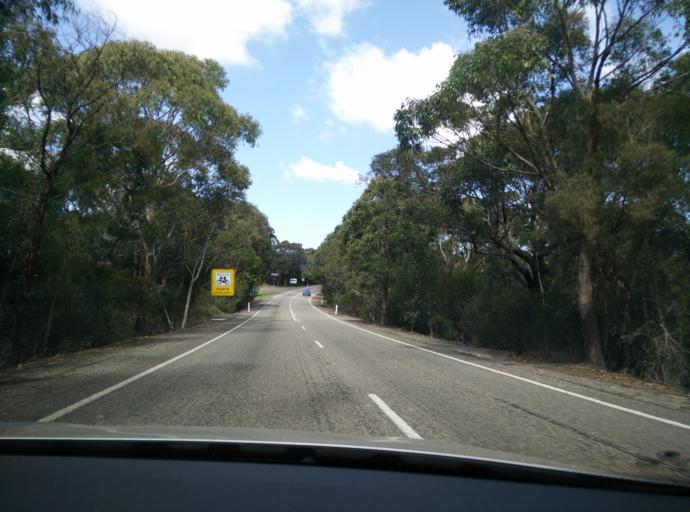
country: AU
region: New South Wales
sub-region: Gosford Shire
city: Point Clare
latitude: -33.4511
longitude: 151.2916
